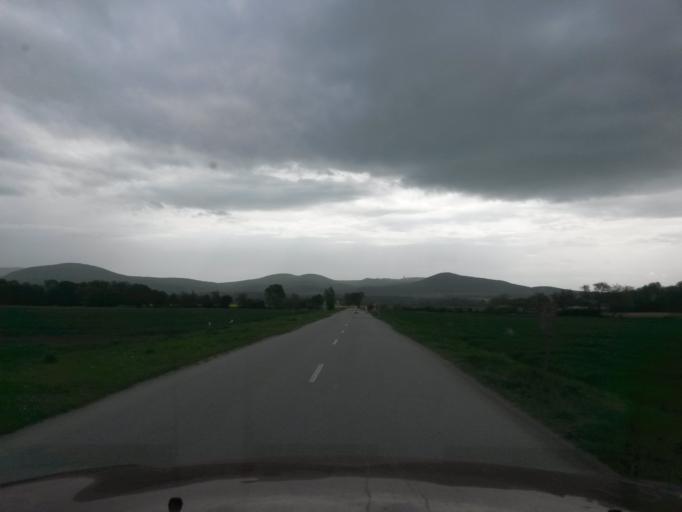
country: HU
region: Borsod-Abauj-Zemplen
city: Gonc
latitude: 48.5442
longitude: 21.2772
